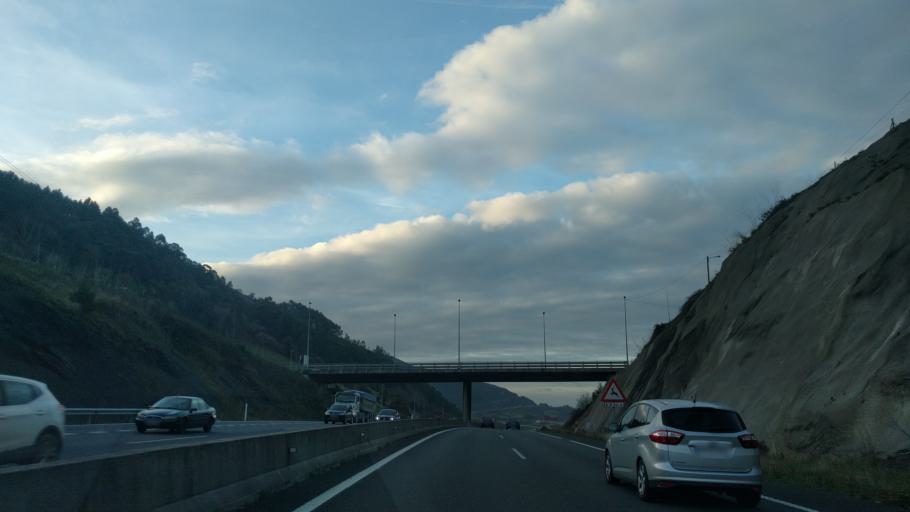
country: ES
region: Basque Country
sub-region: Bizkaia
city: San Julian de Muskiz
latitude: 43.3424
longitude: -3.1549
